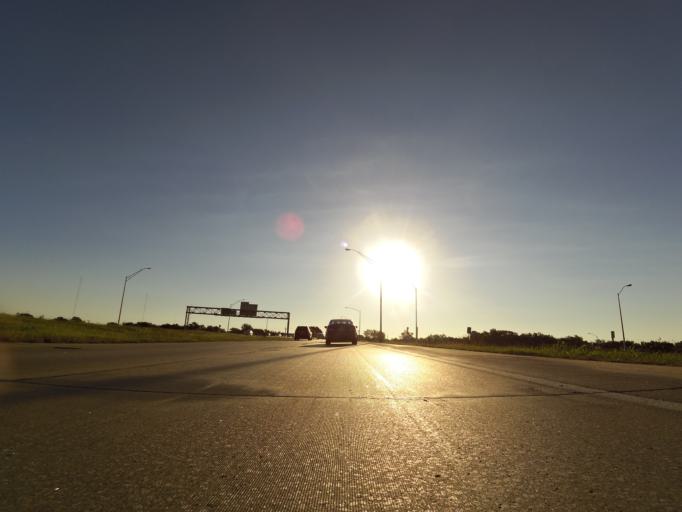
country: US
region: Kansas
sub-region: Sedgwick County
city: Park City
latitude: 37.7565
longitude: -97.3388
